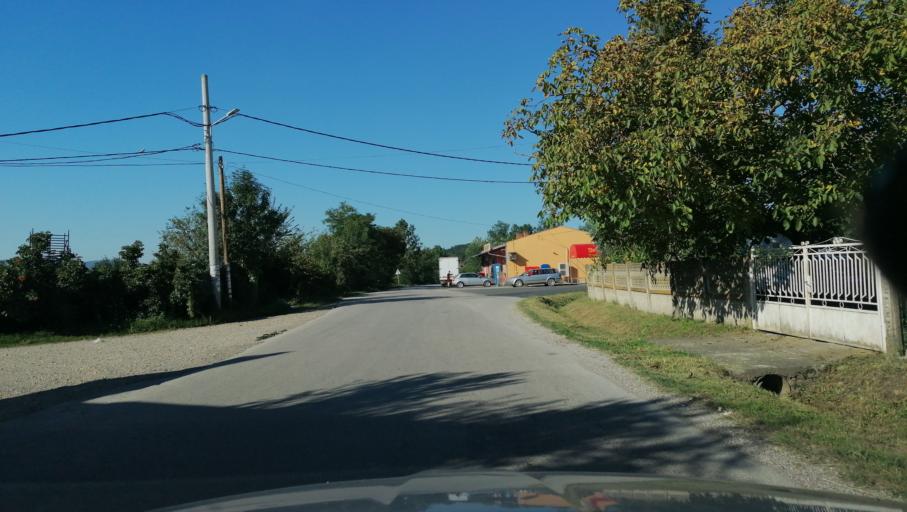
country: RS
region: Central Serbia
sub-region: Sumadijski Okrug
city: Knic
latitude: 43.8422
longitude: 20.6006
